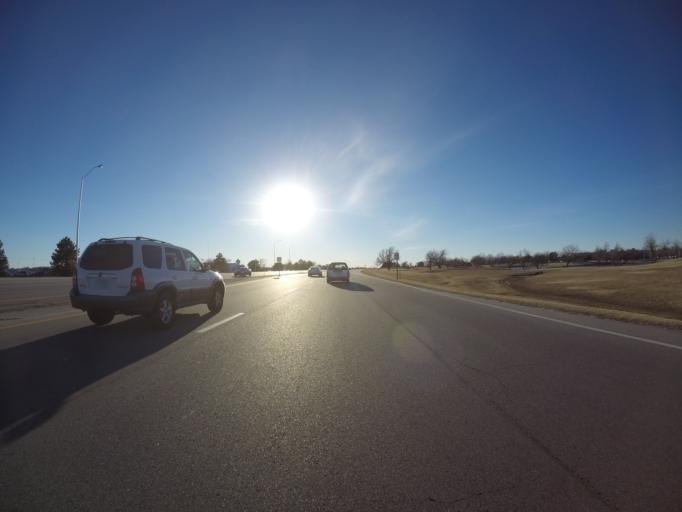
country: US
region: Kansas
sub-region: Sedgwick County
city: Wichita
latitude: 37.6385
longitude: -97.4149
